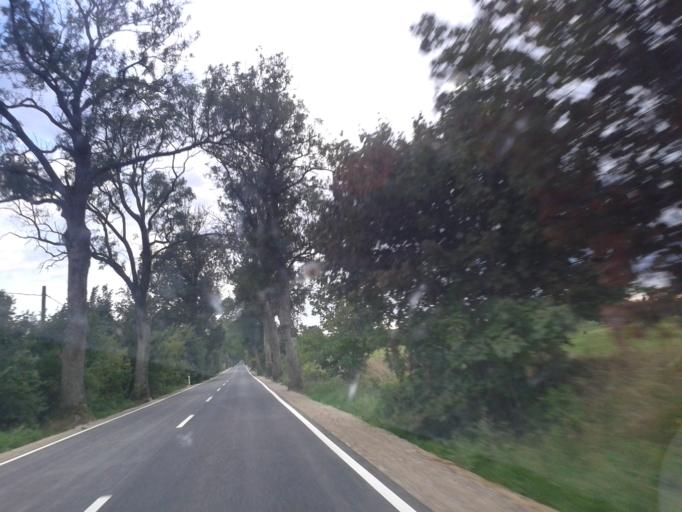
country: PL
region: West Pomeranian Voivodeship
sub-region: Powiat szczecinecki
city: Grzmiaca
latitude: 53.8670
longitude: 16.4839
